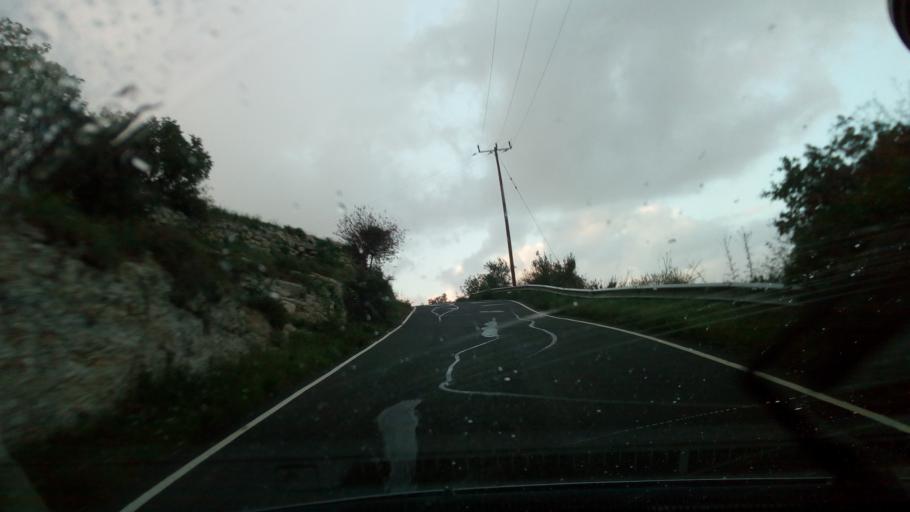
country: CY
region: Pafos
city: Polis
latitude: 34.9540
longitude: 32.4270
